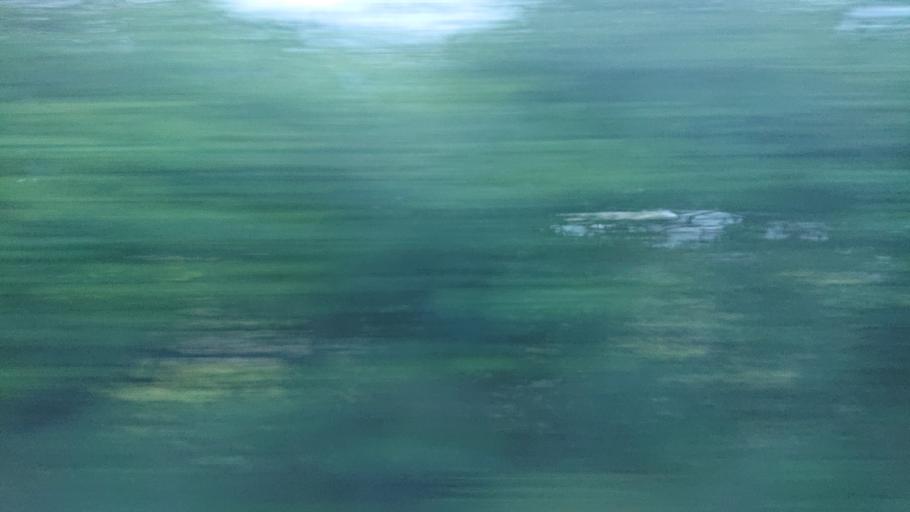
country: TW
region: Taiwan
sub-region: Taitung
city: Taitung
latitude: 23.0410
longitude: 121.1630
